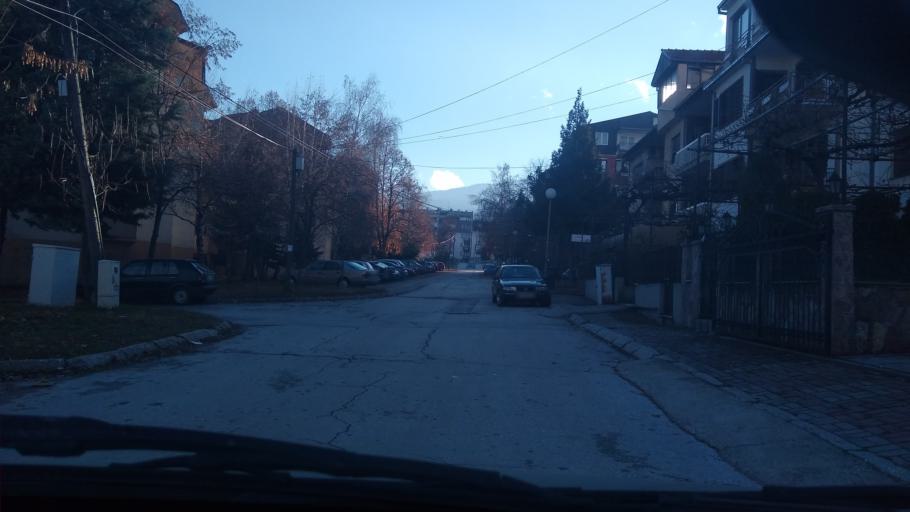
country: MK
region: Bitola
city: Bitola
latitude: 41.0244
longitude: 21.3151
